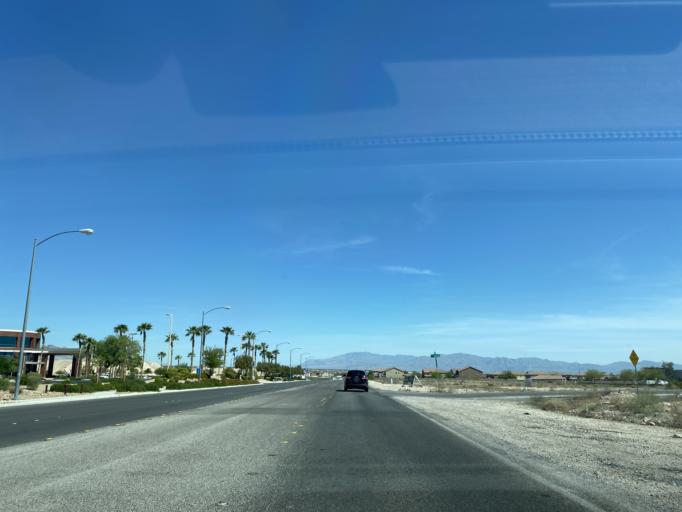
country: US
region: Nevada
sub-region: Clark County
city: Spring Valley
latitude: 36.0715
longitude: -115.2607
